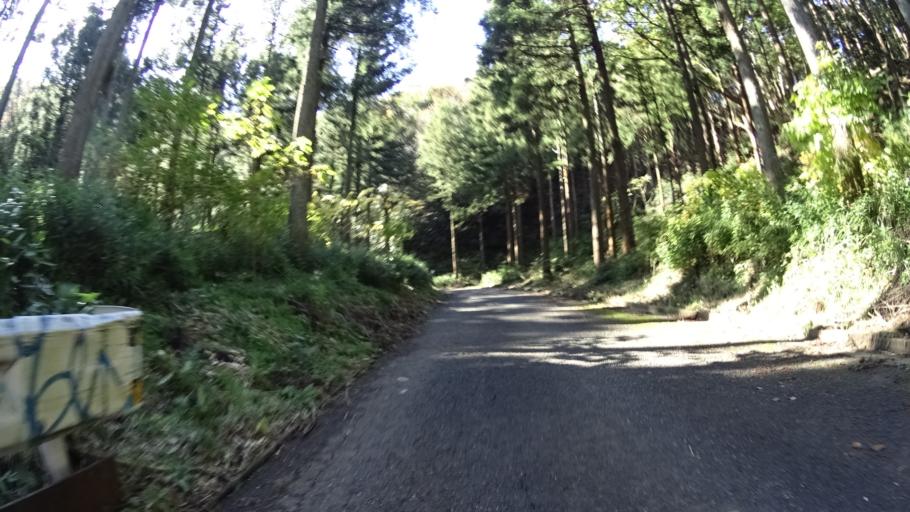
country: JP
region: Kanagawa
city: Zama
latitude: 35.5266
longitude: 139.2724
